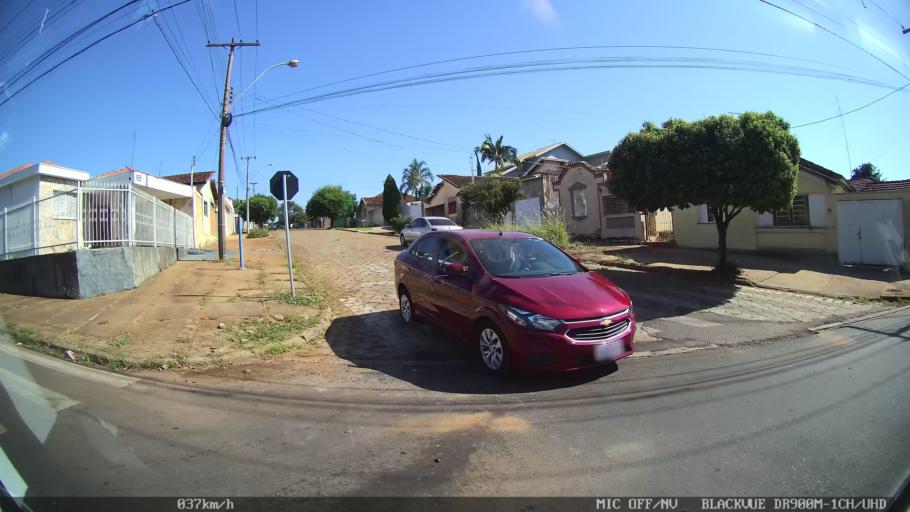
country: BR
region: Sao Paulo
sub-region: Batatais
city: Batatais
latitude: -20.8945
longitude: -47.5816
